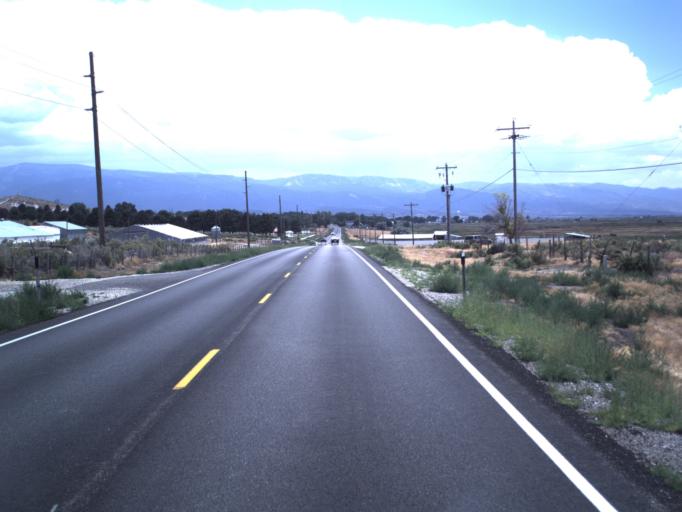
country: US
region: Utah
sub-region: Sanpete County
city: Moroni
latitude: 39.5458
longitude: -111.5976
